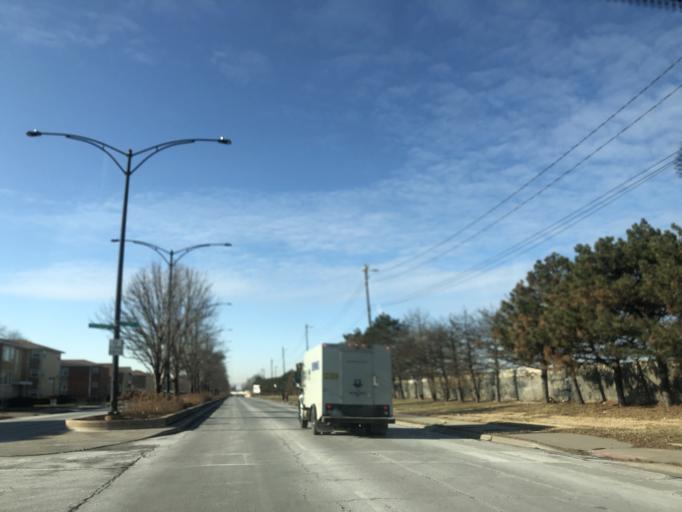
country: US
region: Illinois
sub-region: Cook County
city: Evergreen Park
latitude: 41.7499
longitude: -87.6961
